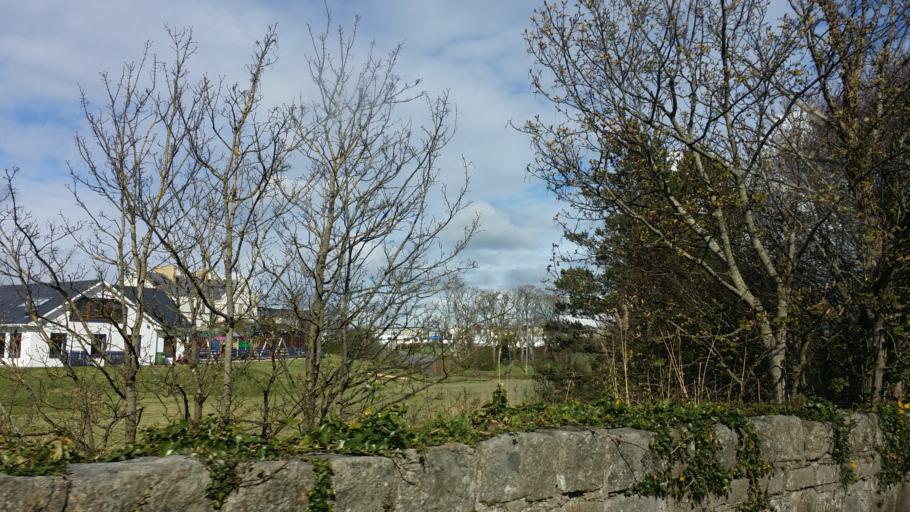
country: IE
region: Ulster
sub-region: County Donegal
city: Bundoran
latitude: 54.4769
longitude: -8.2798
